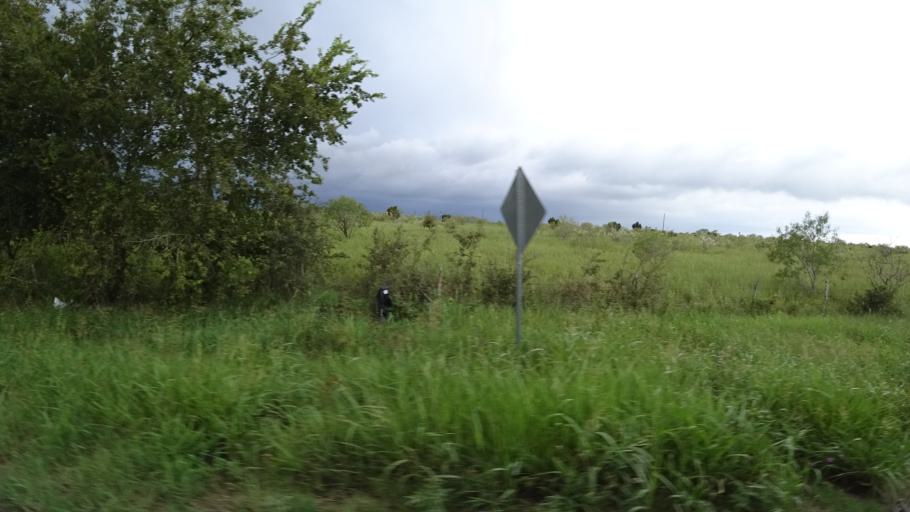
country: US
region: Texas
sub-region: Travis County
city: Onion Creek
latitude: 30.1360
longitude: -97.7166
